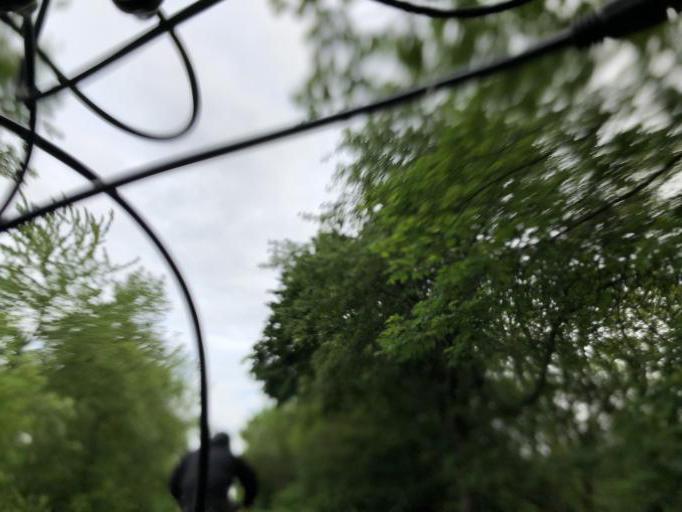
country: DE
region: Bavaria
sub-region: Regierungsbezirk Mittelfranken
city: Erlangen
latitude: 49.5411
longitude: 11.0273
